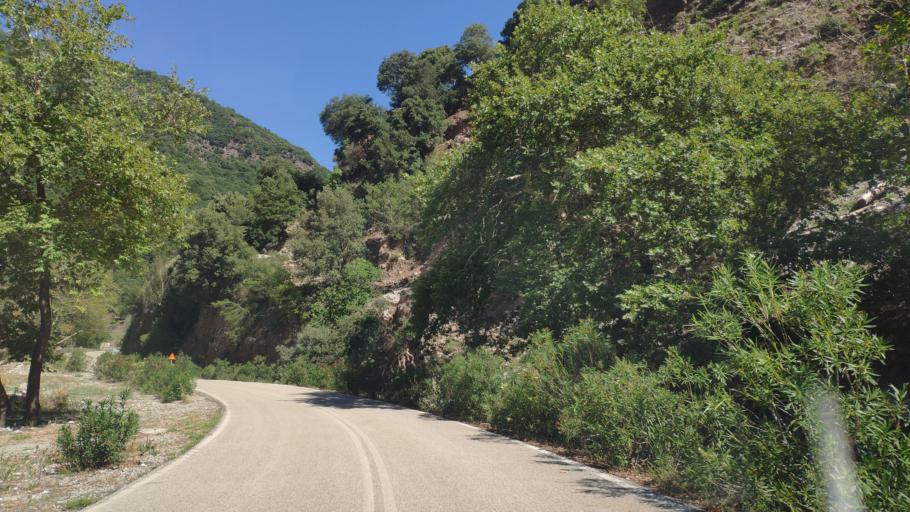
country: GR
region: Central Greece
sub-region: Nomos Evrytanias
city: Kerasochori
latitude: 39.0517
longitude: 21.6029
